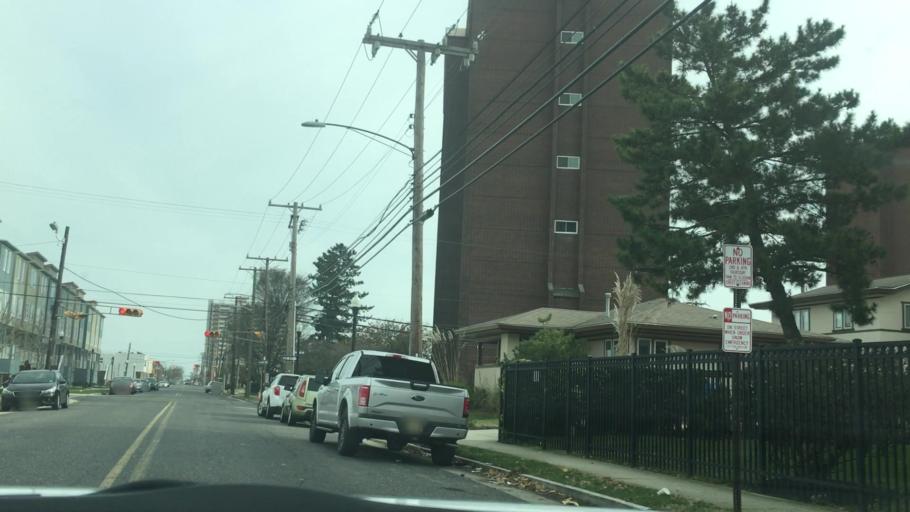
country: US
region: New Jersey
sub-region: Atlantic County
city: Atlantic City
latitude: 39.3660
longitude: -74.4314
